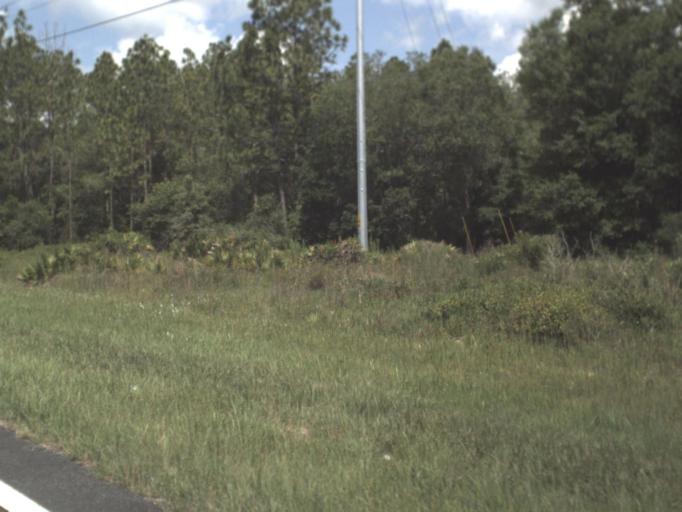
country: US
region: Florida
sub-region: Levy County
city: Chiefland
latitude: 29.2386
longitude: -82.9332
